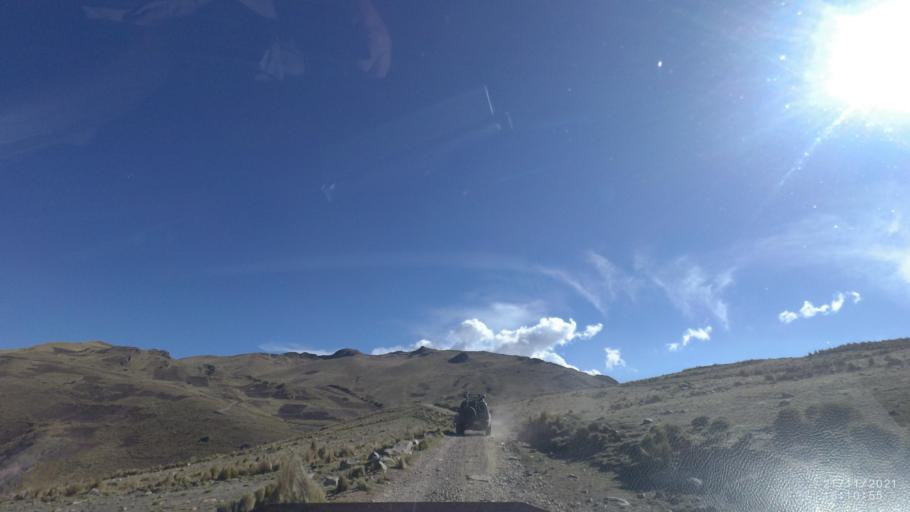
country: BO
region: Cochabamba
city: Cochabamba
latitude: -16.9940
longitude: -66.2706
